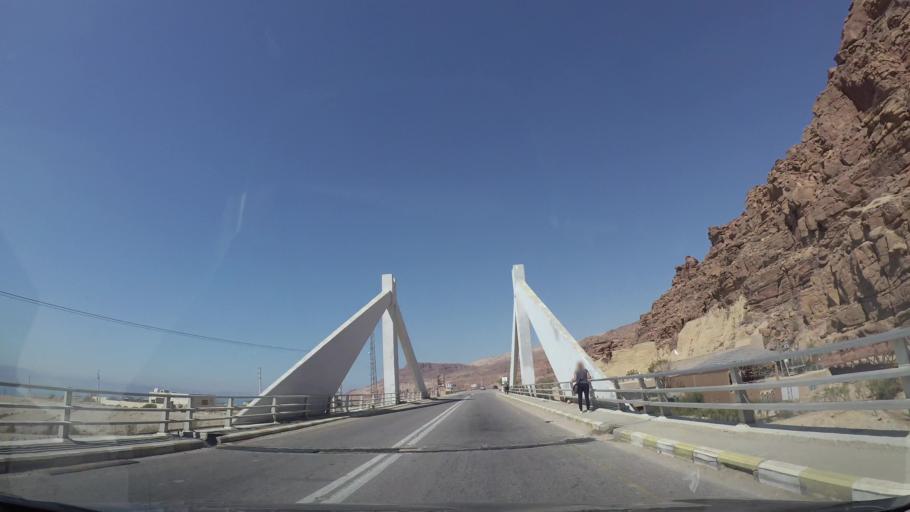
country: JO
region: Karak
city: Al Qasr
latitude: 31.4666
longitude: 35.5727
